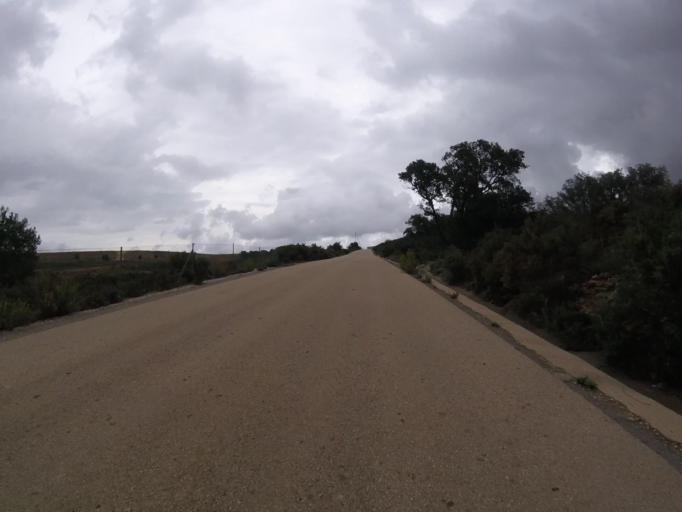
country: ES
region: Valencia
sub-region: Provincia de Castello
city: Benlloch
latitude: 40.2021
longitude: 0.0595
